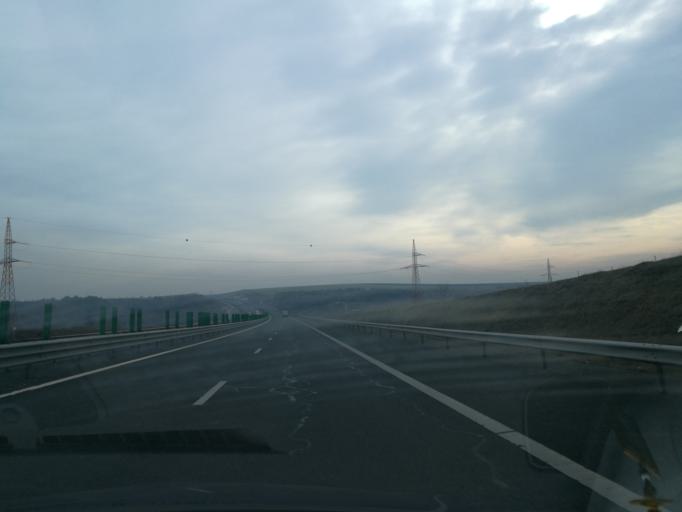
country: RO
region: Constanta
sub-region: Oras Murfatlar
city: Siminoc
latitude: 44.1431
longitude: 28.3660
